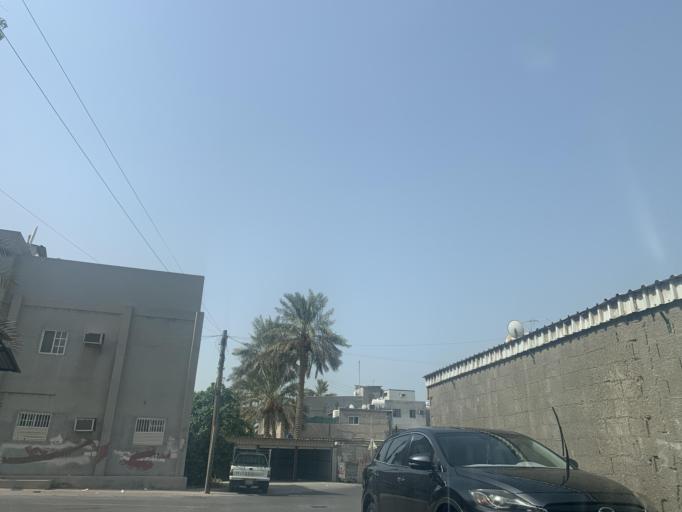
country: BH
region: Manama
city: Jidd Hafs
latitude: 26.2099
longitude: 50.4599
